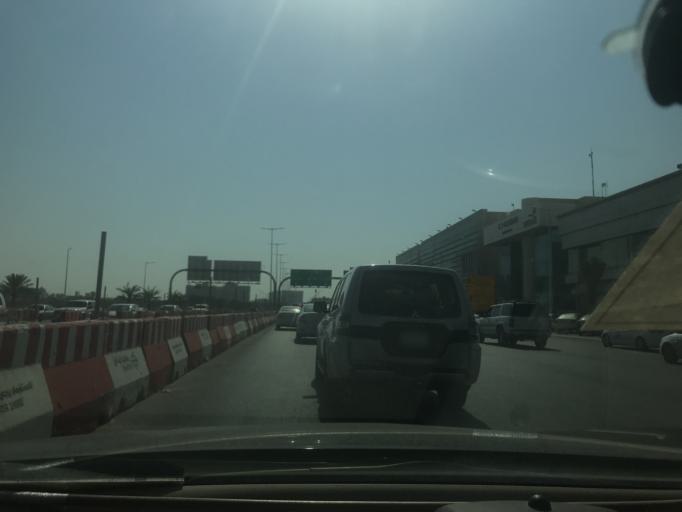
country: SA
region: Ar Riyad
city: Riyadh
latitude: 24.6992
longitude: 46.7229
